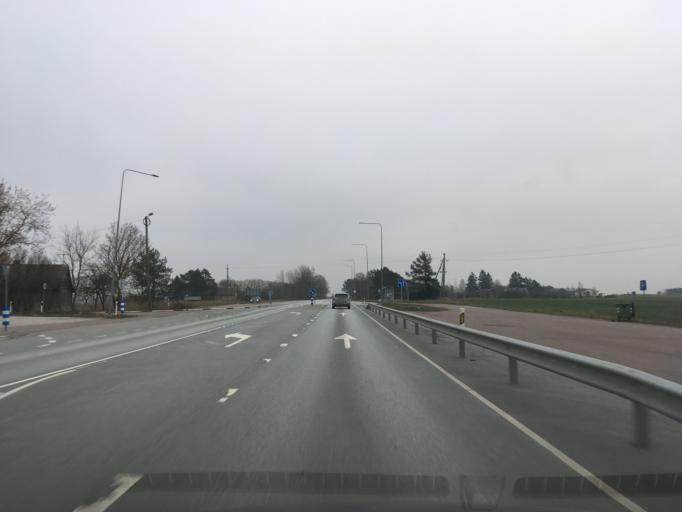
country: EE
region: Ida-Virumaa
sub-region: Puessi linn
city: Pussi
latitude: 59.4121
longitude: 27.0247
